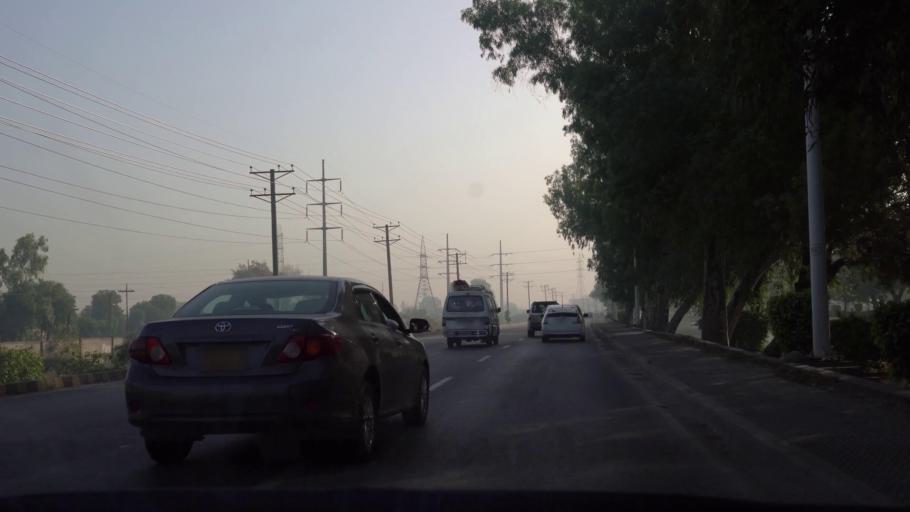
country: PK
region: Punjab
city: Faisalabad
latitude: 31.4484
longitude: 73.1443
